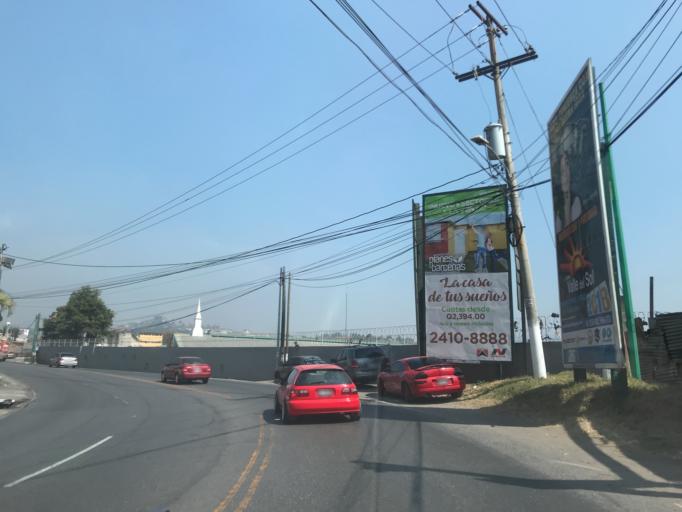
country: GT
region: Guatemala
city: Petapa
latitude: 14.5132
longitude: -90.5643
